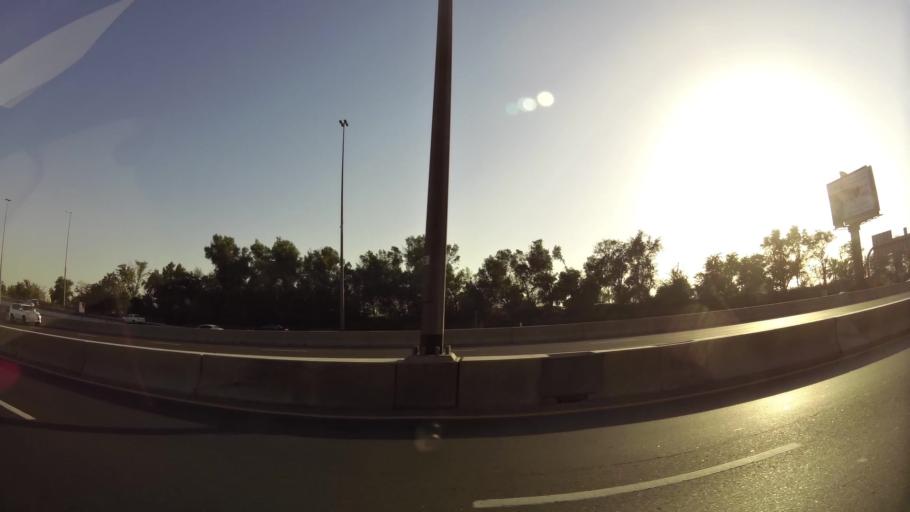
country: AE
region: Ash Shariqah
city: Sharjah
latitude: 25.2436
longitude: 55.3393
